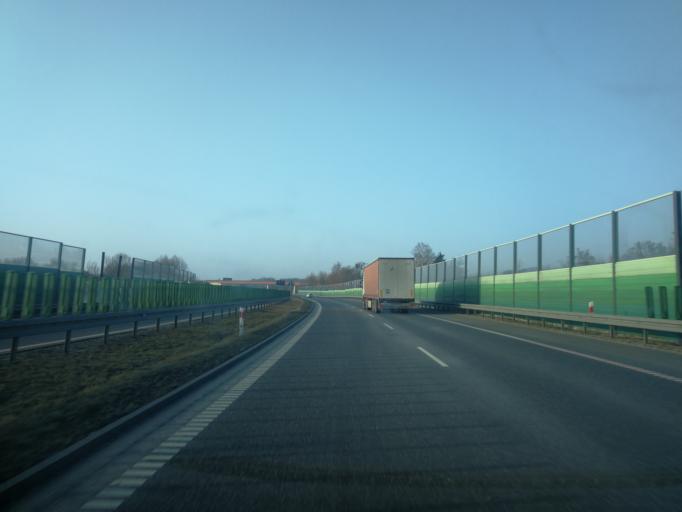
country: PL
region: Warmian-Masurian Voivodeship
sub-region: Powiat elblaski
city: Gronowo Gorne
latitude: 54.1294
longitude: 19.4594
